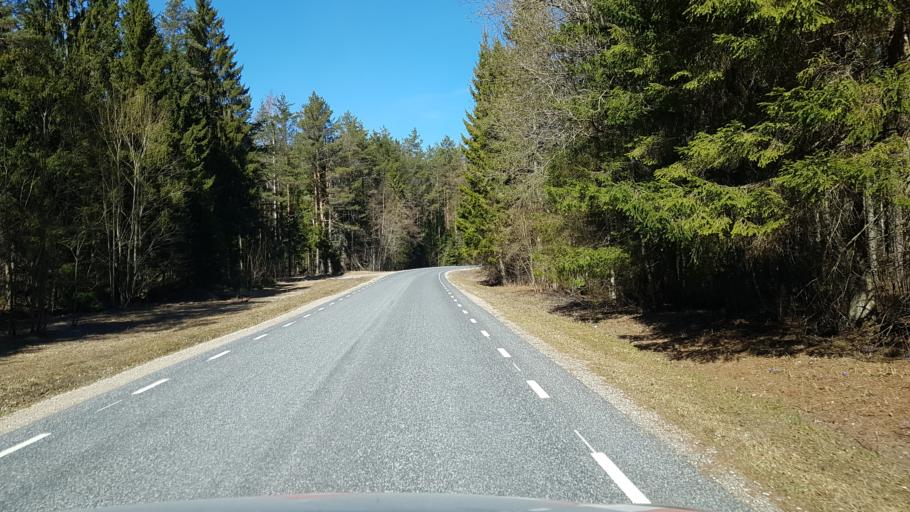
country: EE
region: Laeaene-Virumaa
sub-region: Vinni vald
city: Vinni
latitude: 59.1260
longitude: 26.5210
